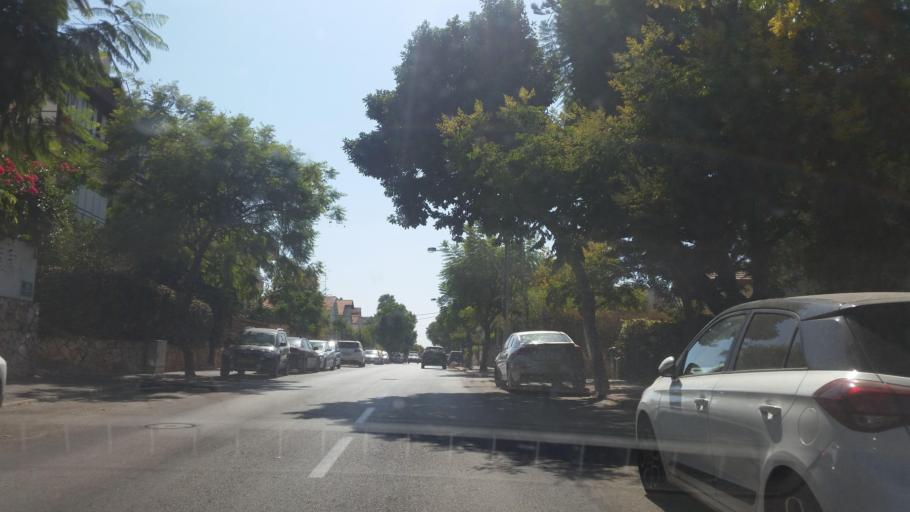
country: IL
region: Central District
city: Ra'anana
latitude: 32.1803
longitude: 34.8850
